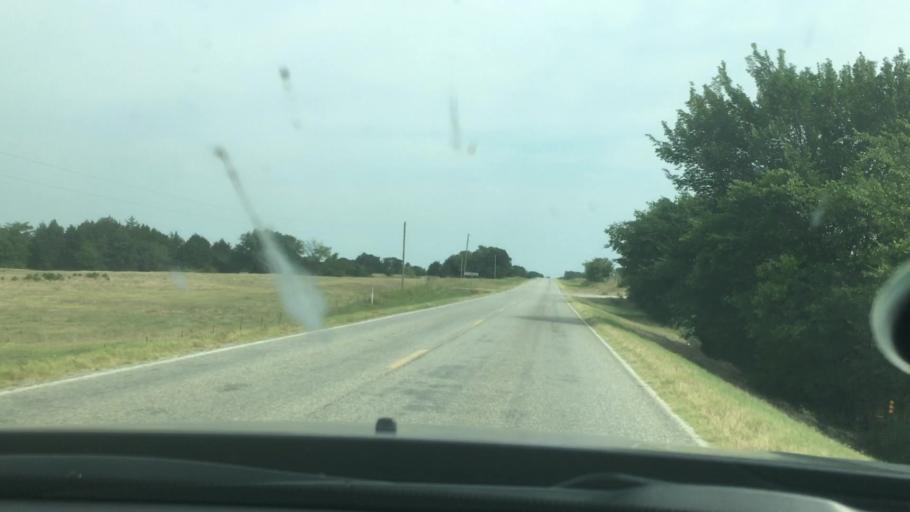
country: US
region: Oklahoma
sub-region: Johnston County
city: Tishomingo
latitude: 34.3086
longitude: -96.4247
